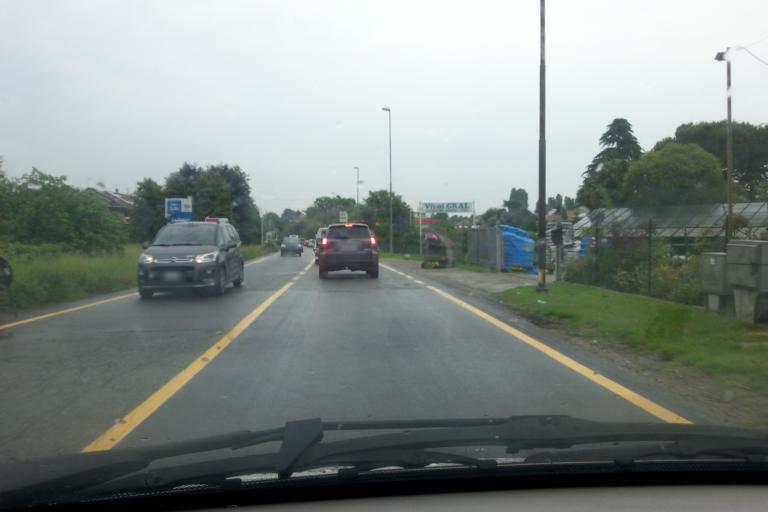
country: IT
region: Piedmont
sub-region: Provincia di Torino
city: Alpignano
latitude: 45.0866
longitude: 7.5221
